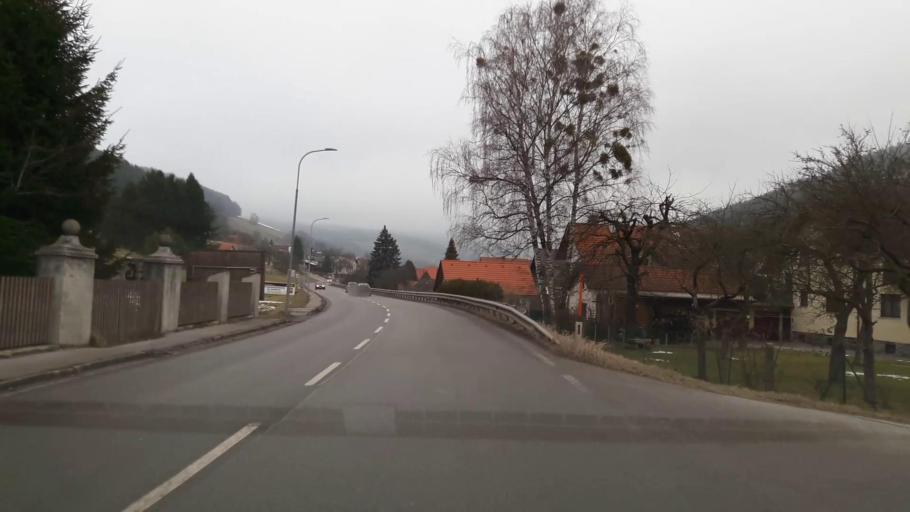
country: AT
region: Lower Austria
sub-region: Politischer Bezirk Neunkirchen
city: Thomasberg
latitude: 47.5713
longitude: 16.0995
